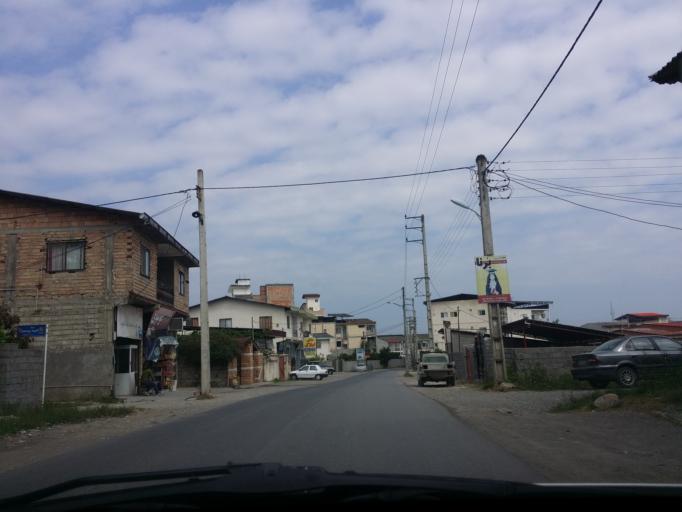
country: IR
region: Mazandaran
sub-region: Nowshahr
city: Nowshahr
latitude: 36.6273
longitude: 51.4854
